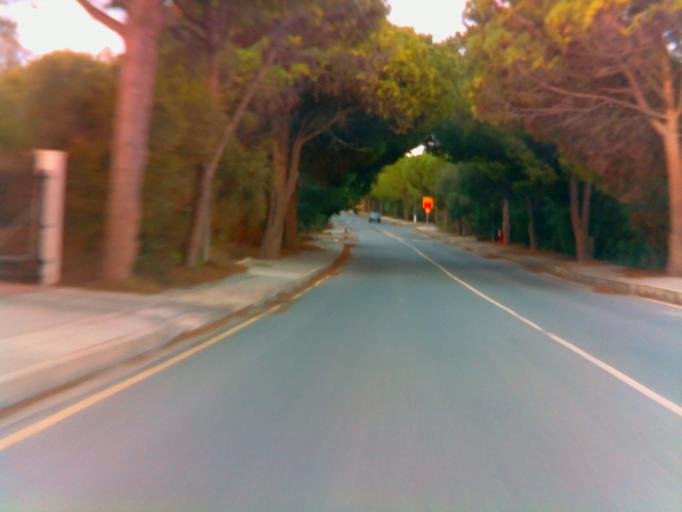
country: CY
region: Pafos
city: Pegeia
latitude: 34.8543
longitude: 32.3715
